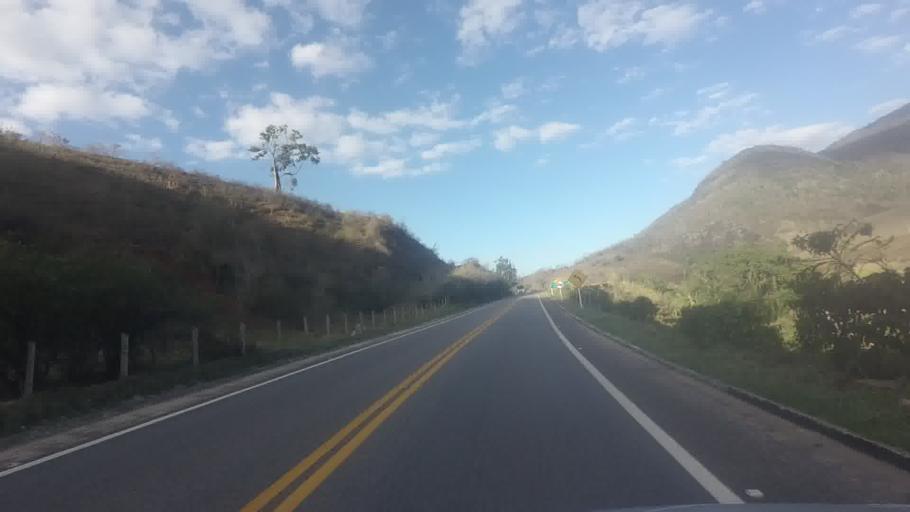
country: BR
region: Espirito Santo
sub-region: Mimoso Do Sul
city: Mimoso do Sul
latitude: -20.9220
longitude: -41.3113
